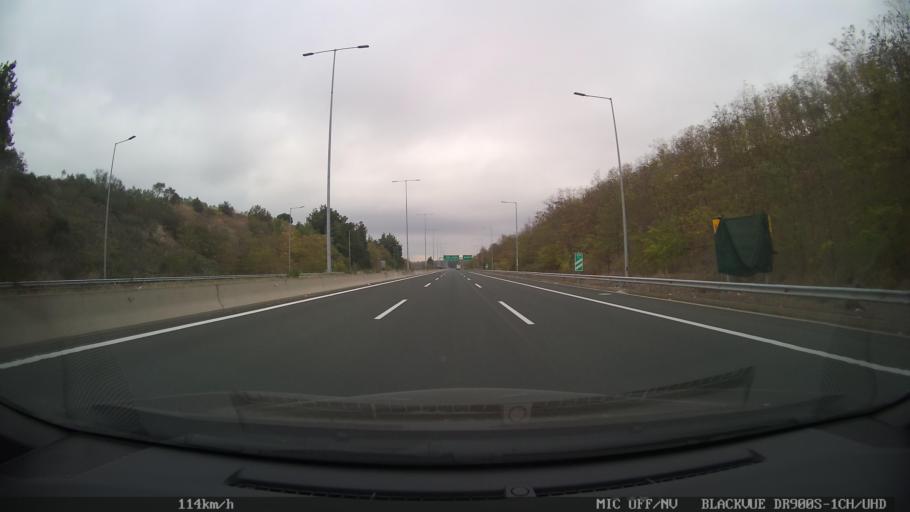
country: GR
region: Central Macedonia
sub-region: Nomos Pierias
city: Makrygialos
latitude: 40.4243
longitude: 22.5895
